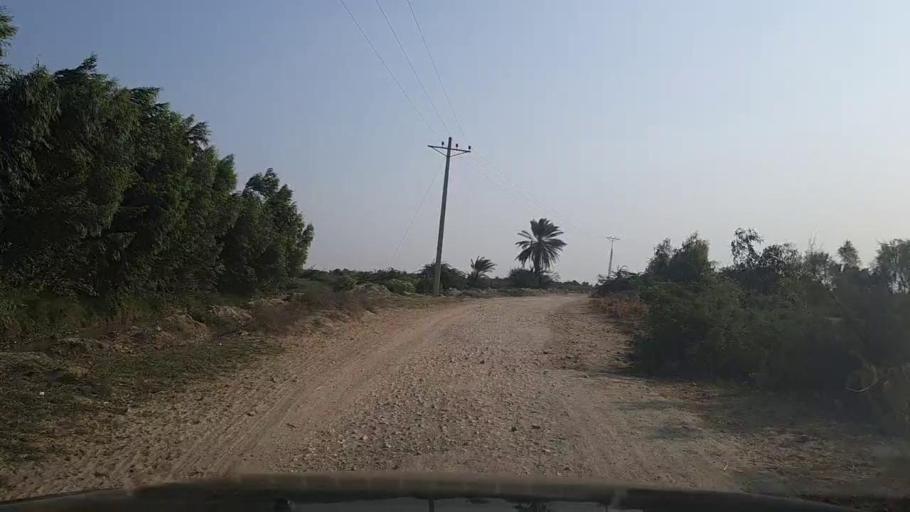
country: PK
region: Sindh
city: Mirpur Sakro
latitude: 24.6324
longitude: 67.7565
